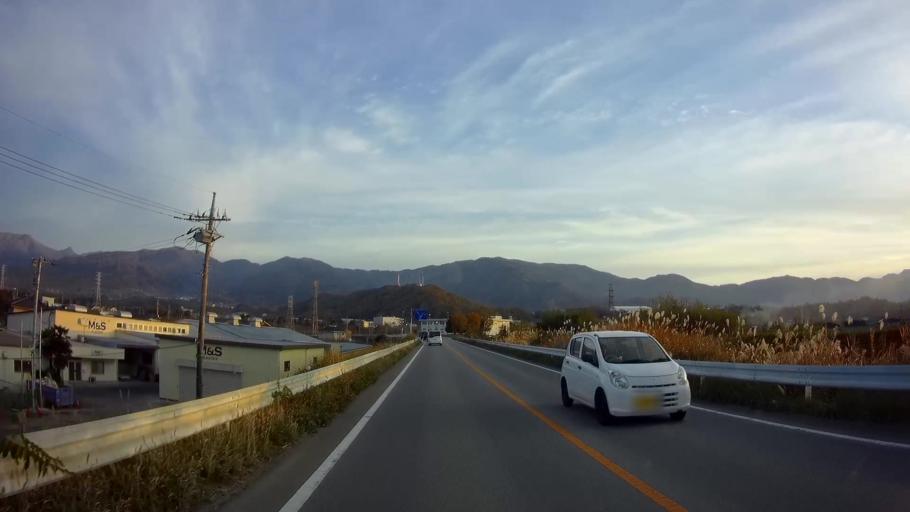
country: JP
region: Yamanashi
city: Isawa
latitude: 35.6099
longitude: 138.6068
